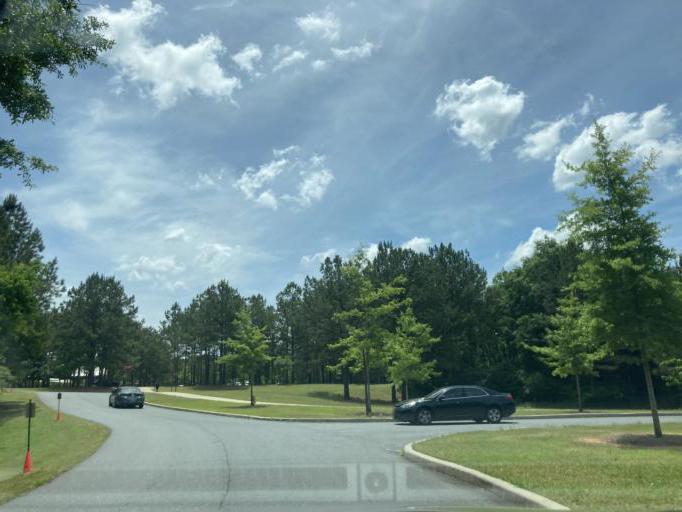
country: US
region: Georgia
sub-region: Bibb County
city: Macon
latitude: 32.8757
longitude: -83.6548
